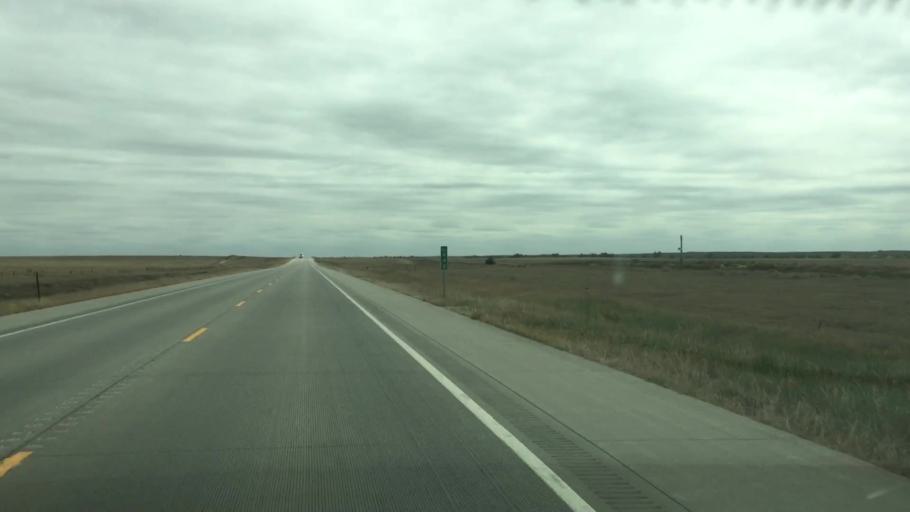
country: US
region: Colorado
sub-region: Kiowa County
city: Eads
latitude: 38.7771
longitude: -102.8887
